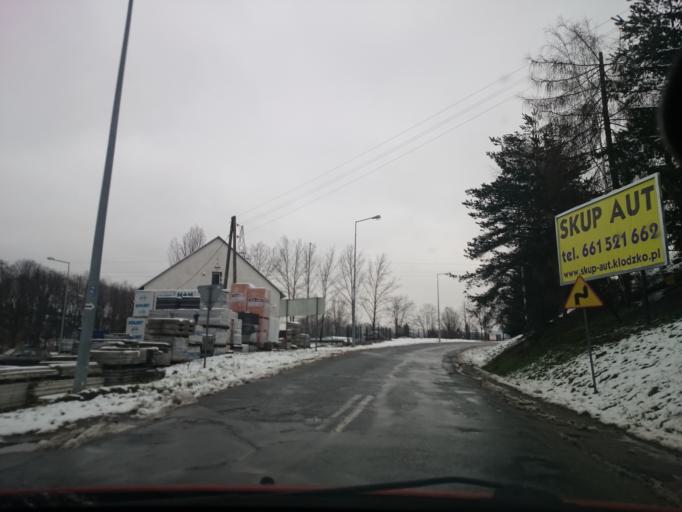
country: PL
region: Lower Silesian Voivodeship
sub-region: Powiat klodzki
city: Bystrzyca Klodzka
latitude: 50.3043
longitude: 16.6559
